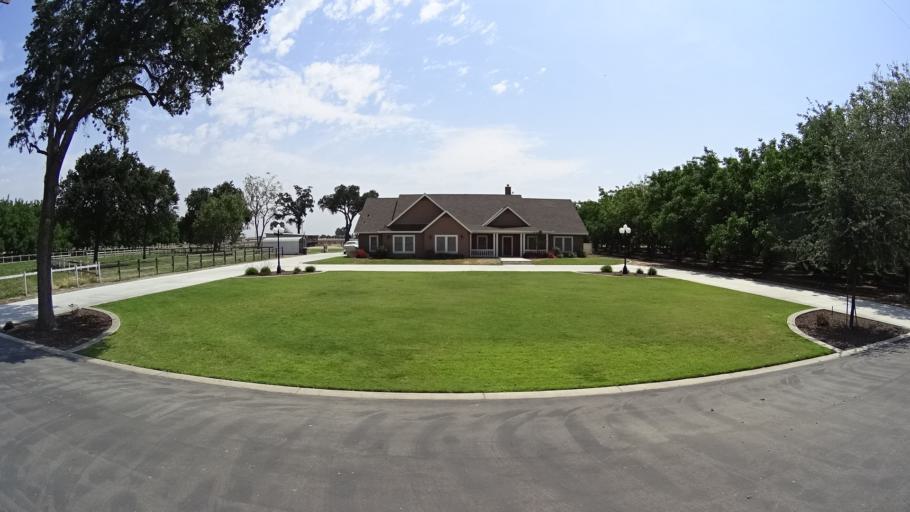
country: US
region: California
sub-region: Kings County
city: Lemoore
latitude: 36.3695
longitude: -119.7631
